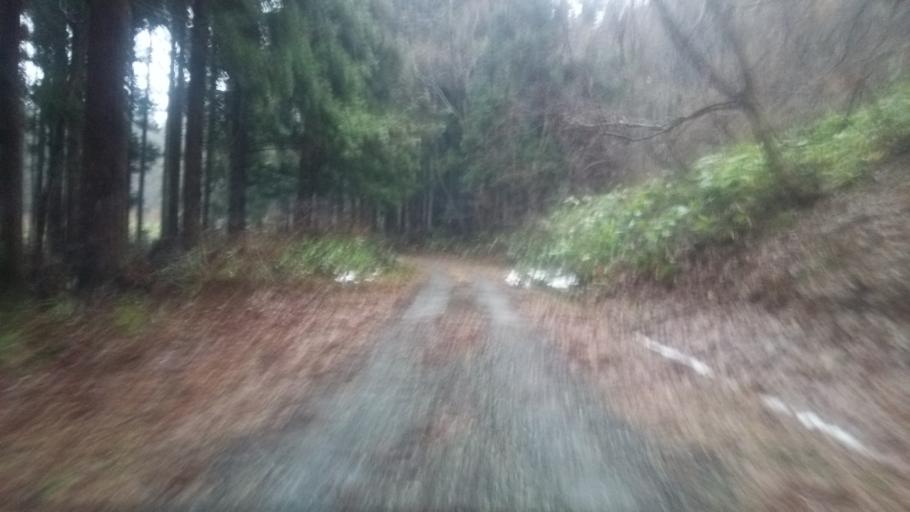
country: JP
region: Fukushima
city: Kitakata
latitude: 37.5767
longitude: 139.9791
